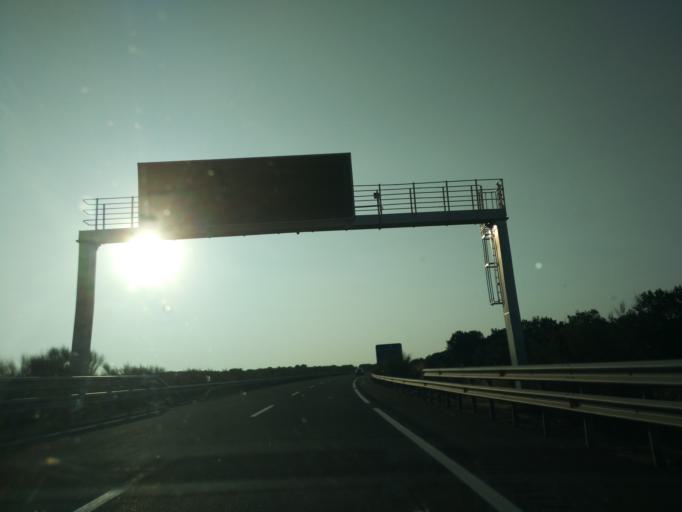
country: ES
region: Castille and Leon
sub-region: Provincia de Avila
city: Berrocalejo de Aragona
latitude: 40.6751
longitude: -4.6214
